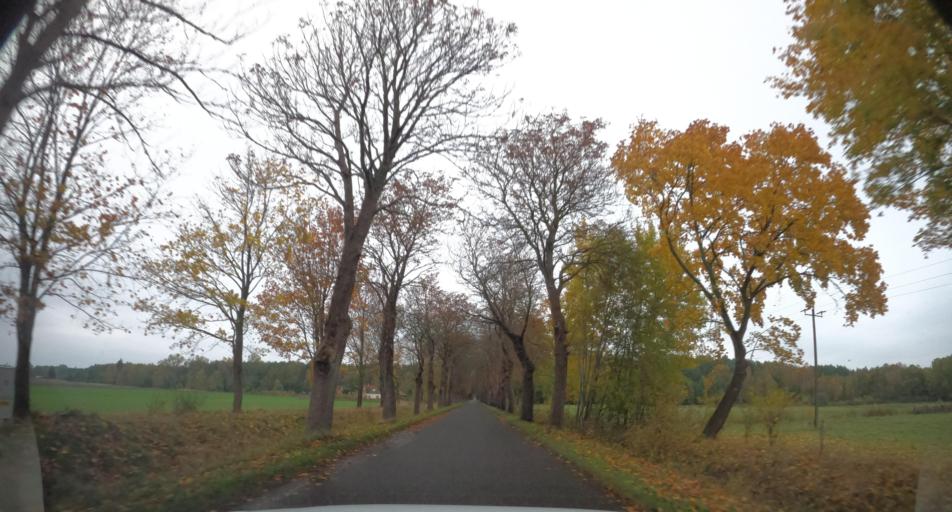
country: PL
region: West Pomeranian Voivodeship
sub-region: Powiat kamienski
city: Wolin
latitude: 53.9345
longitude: 14.6094
